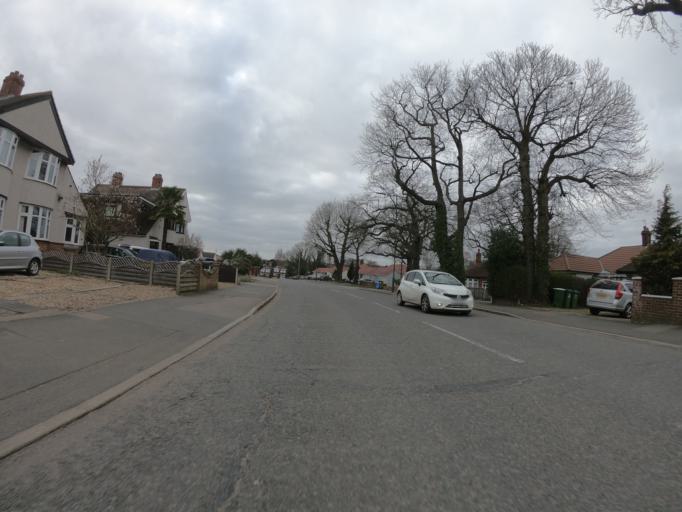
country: GB
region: England
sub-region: Greater London
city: Belvedere
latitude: 51.4787
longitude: 0.1601
